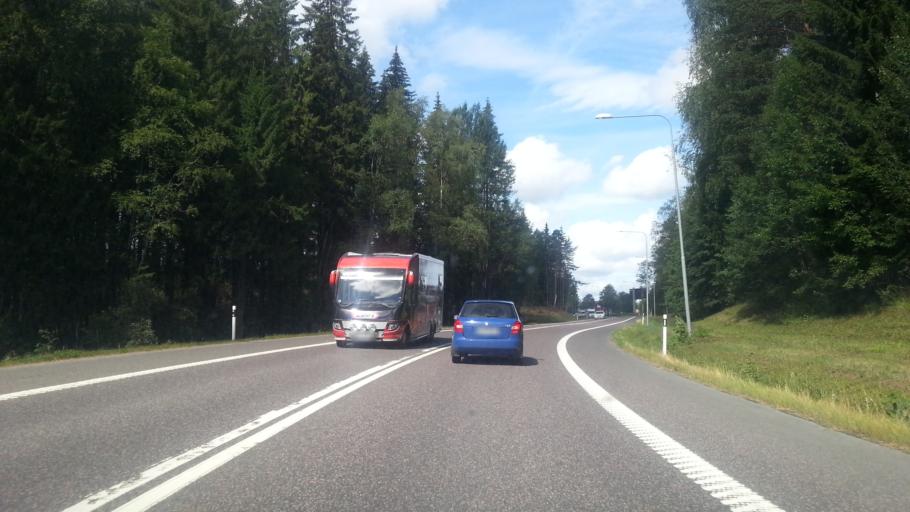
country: SE
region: Dalarna
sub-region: Ludvika Kommun
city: Grangesberg
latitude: 60.0773
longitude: 15.0301
